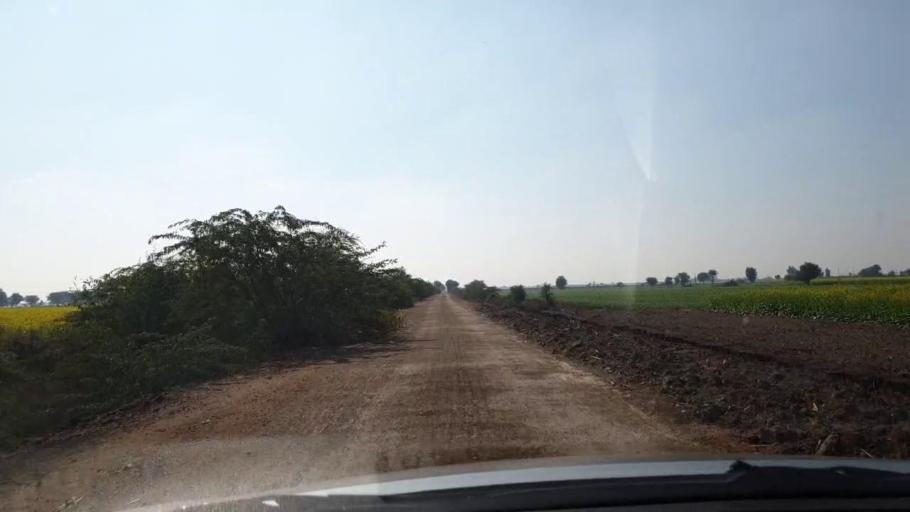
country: PK
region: Sindh
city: Jhol
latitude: 25.8814
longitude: 68.8953
